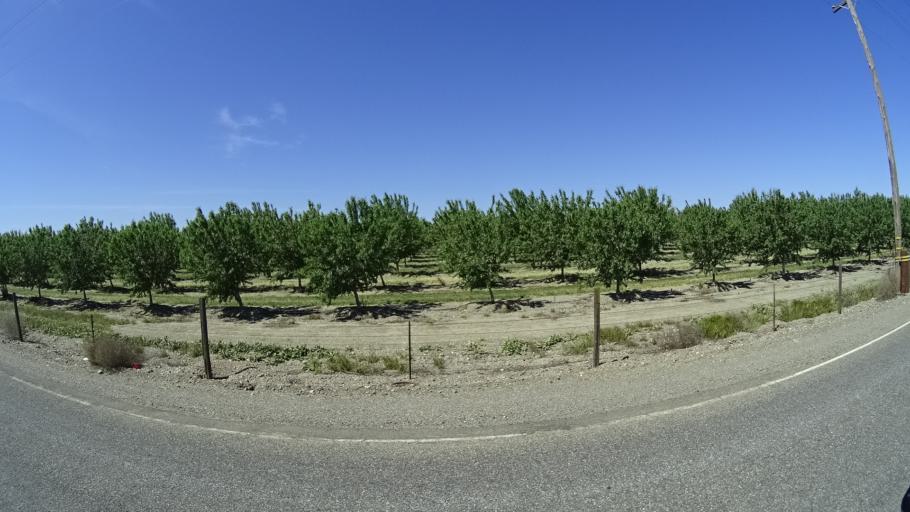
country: US
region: California
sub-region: Glenn County
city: Orland
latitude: 39.6713
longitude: -122.1782
